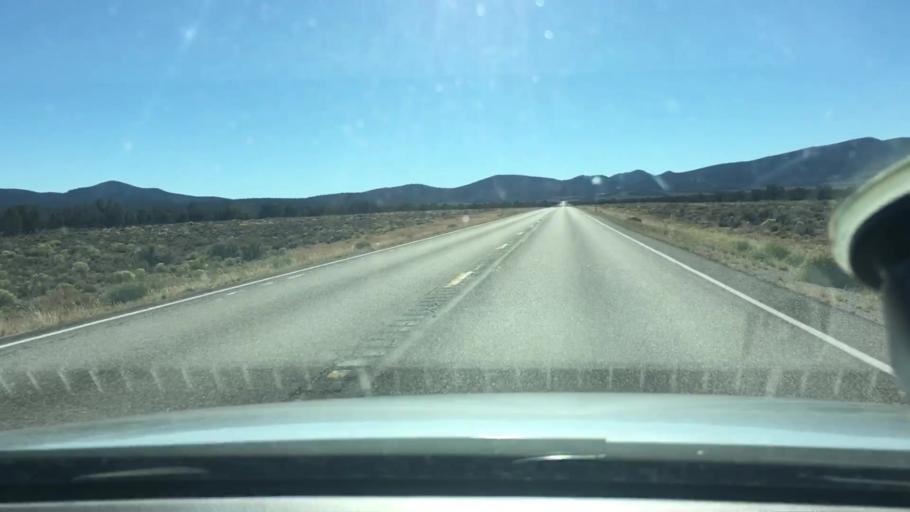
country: US
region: Nevada
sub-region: White Pine County
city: Ely
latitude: 38.8614
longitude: -115.2300
